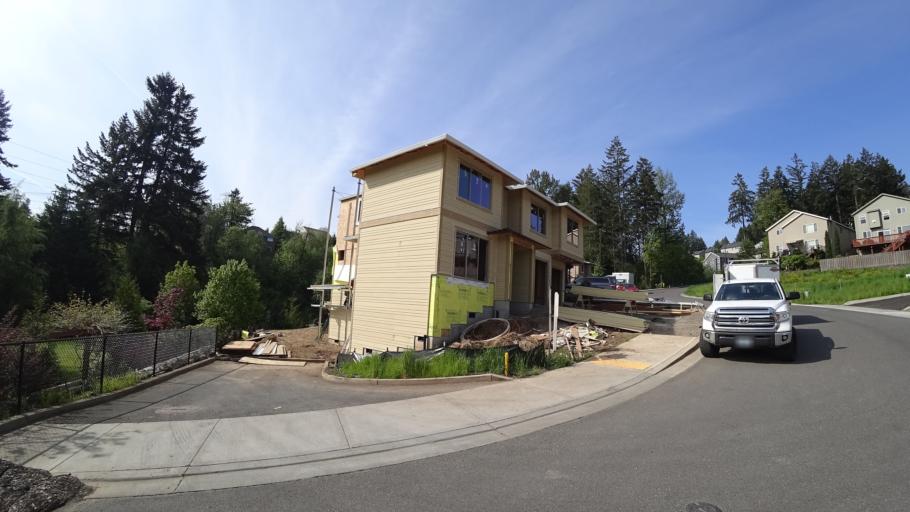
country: US
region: Oregon
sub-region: Washington County
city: Aloha
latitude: 45.4527
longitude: -122.8424
